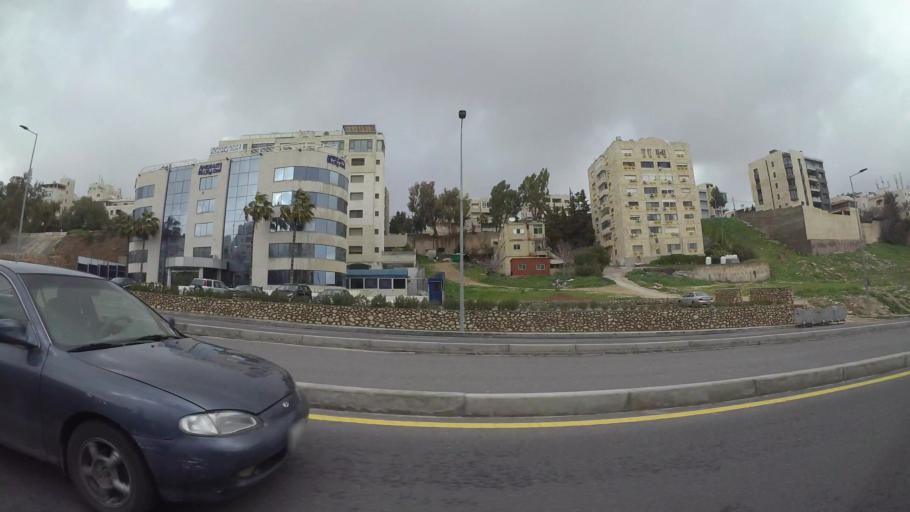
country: JO
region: Amman
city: Amman
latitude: 31.9529
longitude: 35.8903
